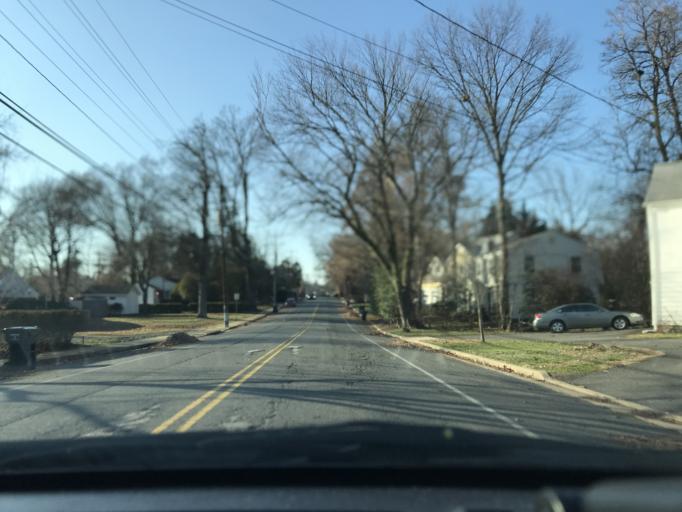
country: US
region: Virginia
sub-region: City of Falls Church
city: Falls Church
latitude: 38.8912
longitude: -77.1760
